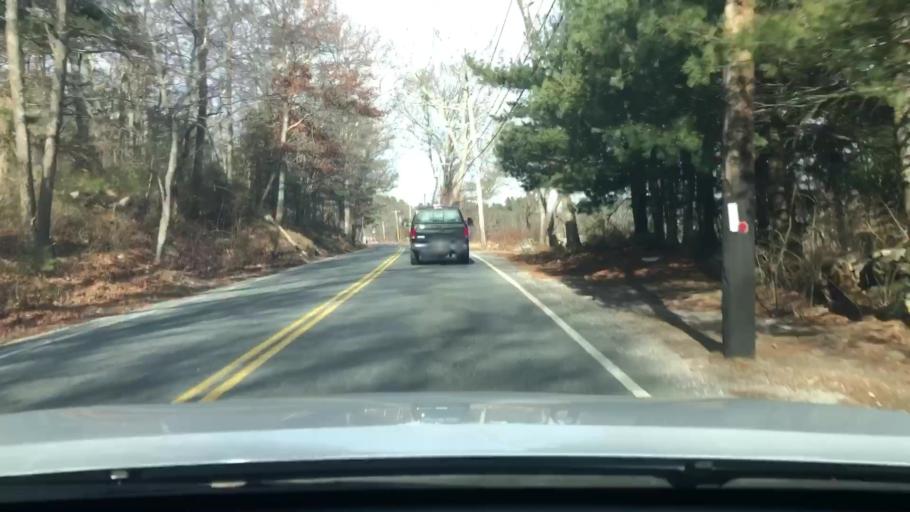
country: US
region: Massachusetts
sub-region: Worcester County
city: Mendon
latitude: 42.0814
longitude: -71.5290
